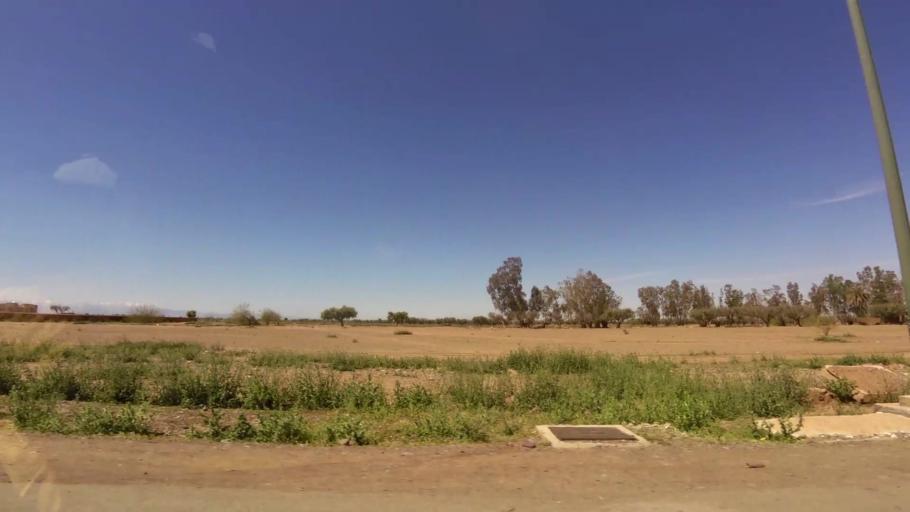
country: MA
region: Marrakech-Tensift-Al Haouz
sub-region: Marrakech
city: Marrakesh
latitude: 31.5665
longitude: -7.9809
